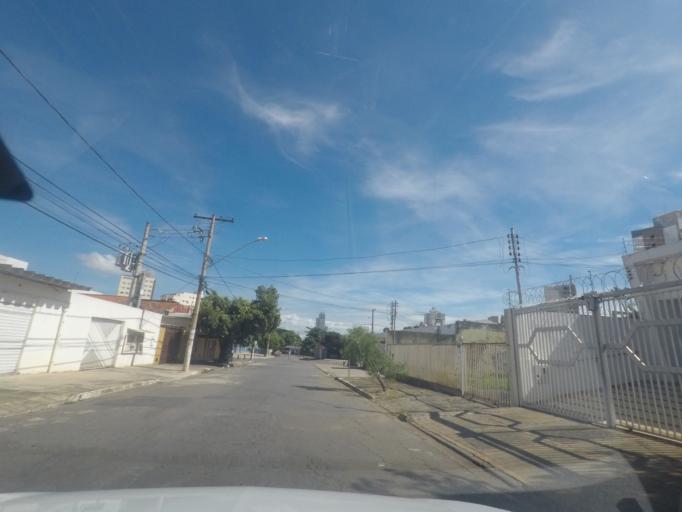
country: BR
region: Goias
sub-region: Goiania
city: Goiania
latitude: -16.6752
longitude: -49.2661
